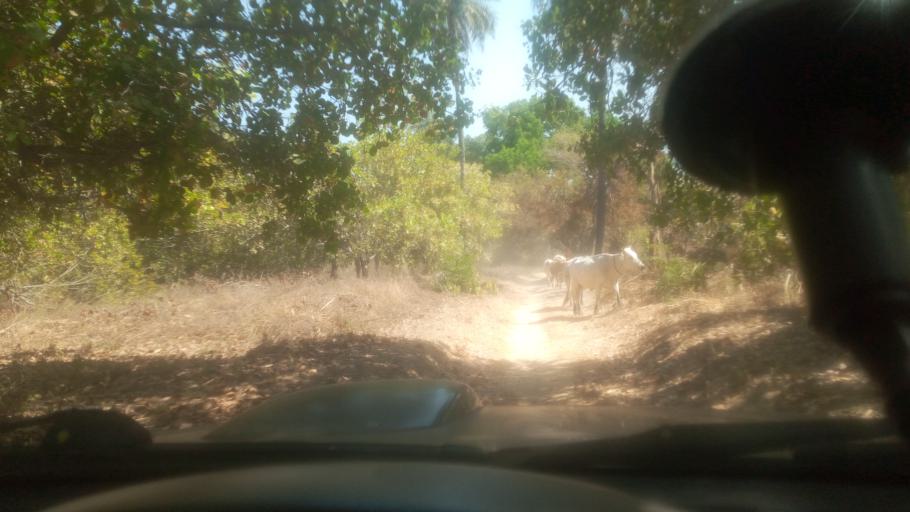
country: GW
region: Oio
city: Farim
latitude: 12.4776
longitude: -15.4068
